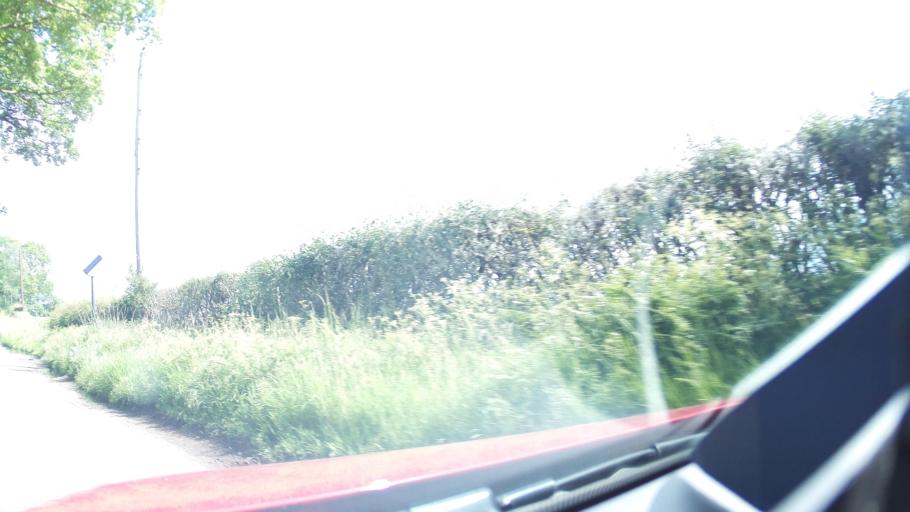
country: GB
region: England
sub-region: Hertfordshire
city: Chorleywood
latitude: 51.6566
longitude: -0.4716
